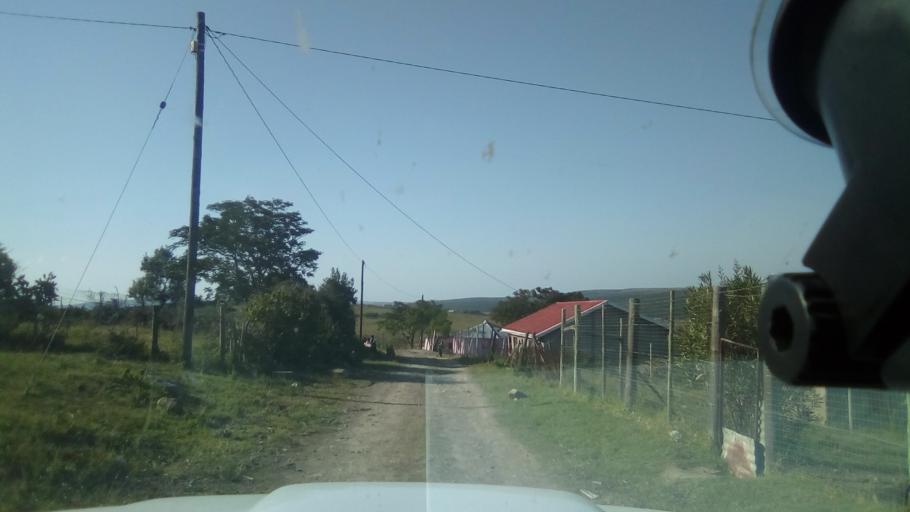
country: ZA
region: Eastern Cape
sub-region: Buffalo City Metropolitan Municipality
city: Bhisho
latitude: -32.8102
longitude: 27.3548
